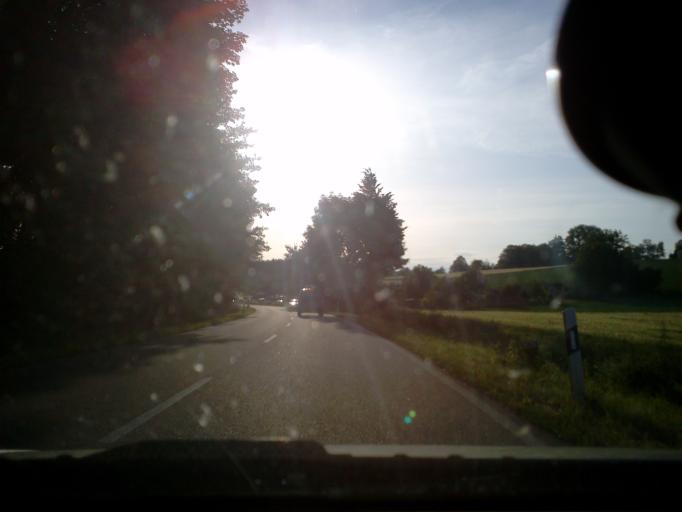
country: DE
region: Baden-Wuerttemberg
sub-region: Karlsruhe Region
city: Woessingen
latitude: 49.0087
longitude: 8.6248
